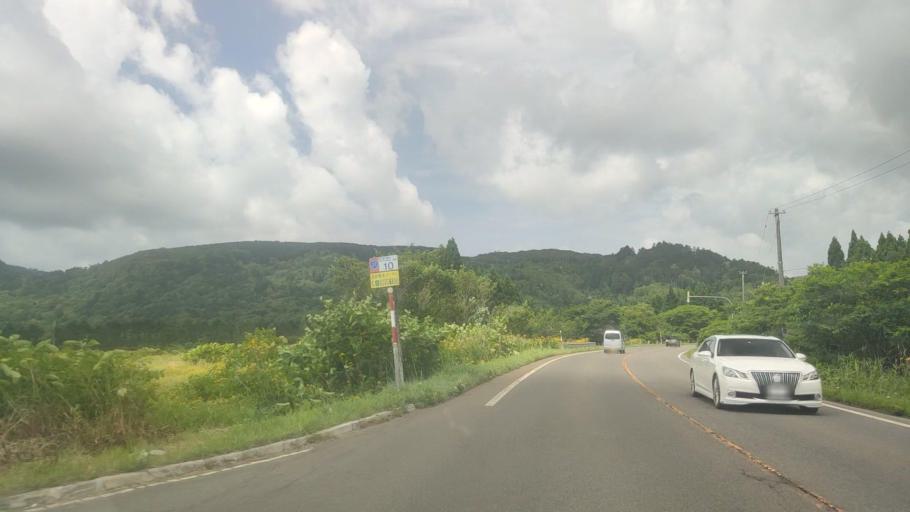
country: JP
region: Hokkaido
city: Niseko Town
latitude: 42.5863
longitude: 140.4498
